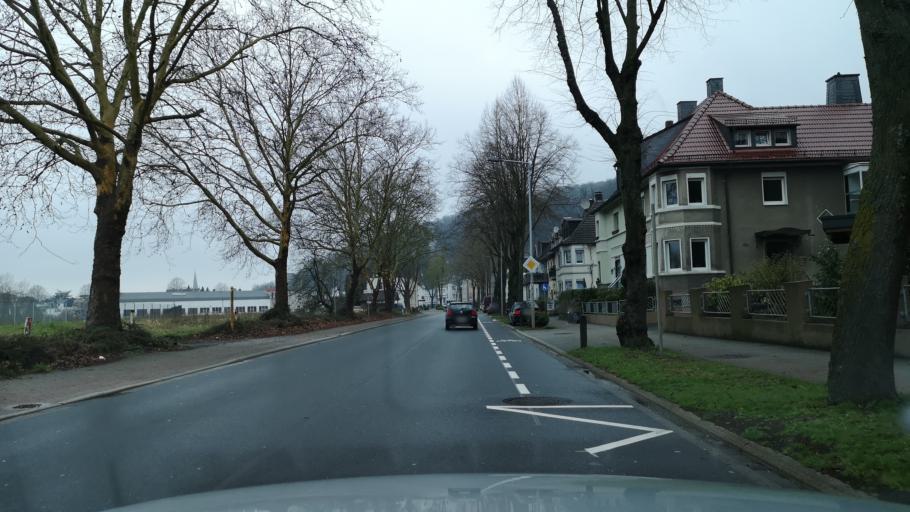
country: DE
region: North Rhine-Westphalia
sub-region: Regierungsbezirk Arnsberg
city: Menden
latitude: 51.4306
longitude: 7.8090
